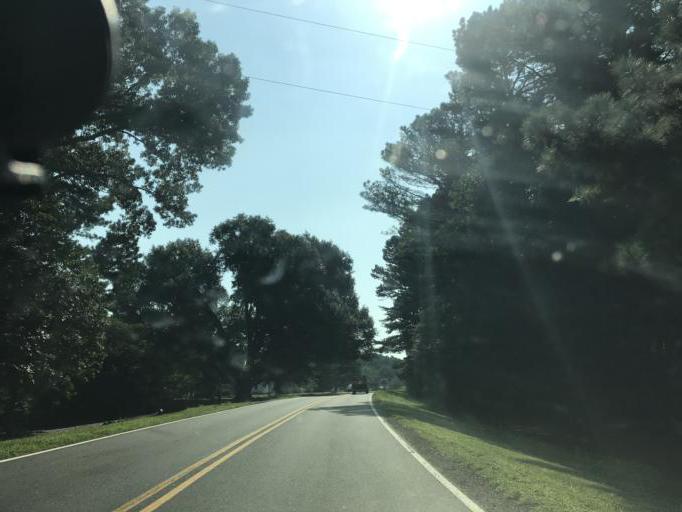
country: US
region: Georgia
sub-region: Forsyth County
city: Cumming
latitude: 34.2624
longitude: -84.1182
